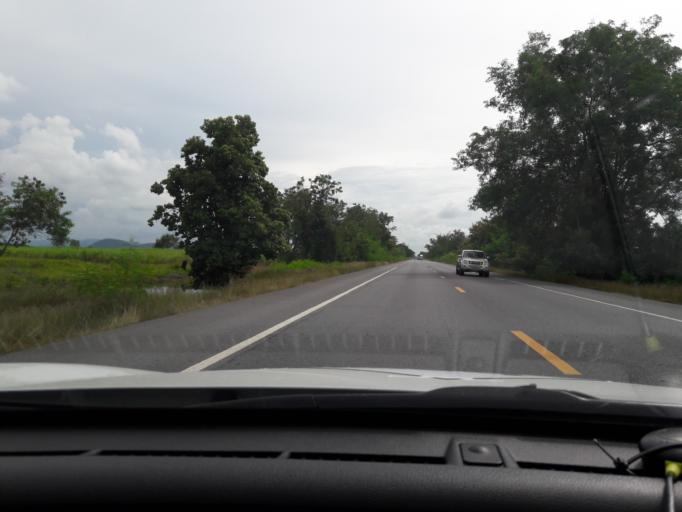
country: TH
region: Nakhon Sawan
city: Phai Sali
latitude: 15.5335
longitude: 100.5502
